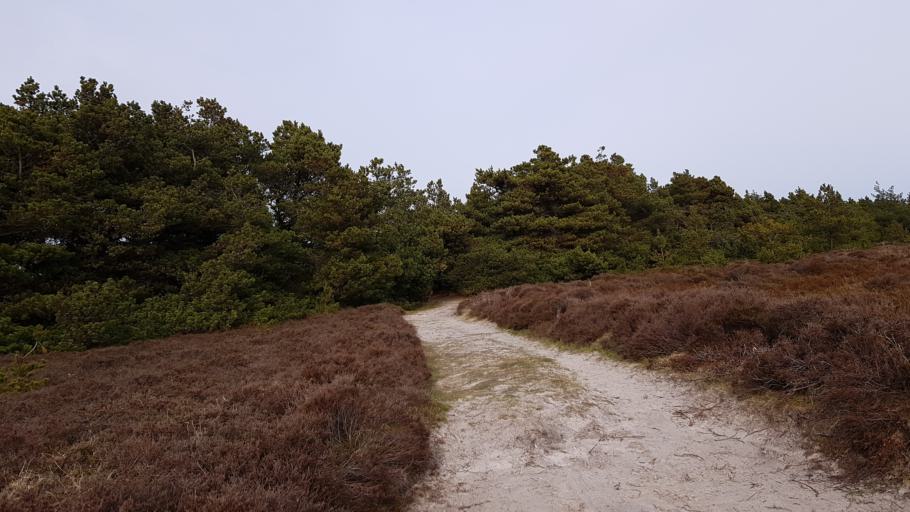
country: DE
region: Schleswig-Holstein
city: List
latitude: 55.1615
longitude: 8.5353
